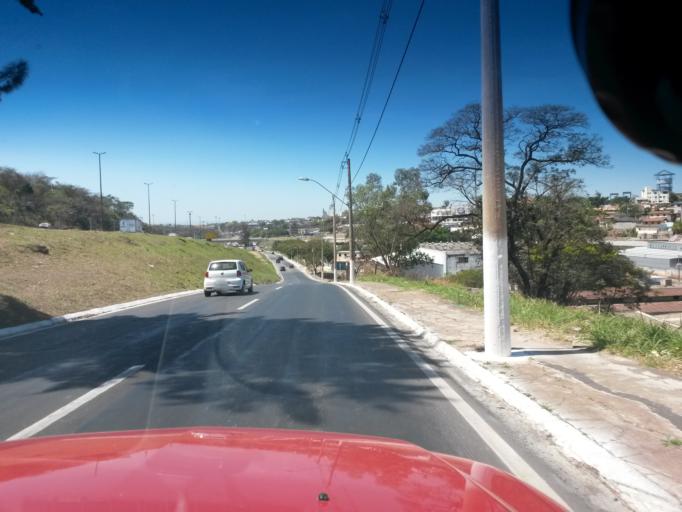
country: BR
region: Minas Gerais
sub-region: Belo Horizonte
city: Belo Horizonte
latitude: -19.8910
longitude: -43.9739
